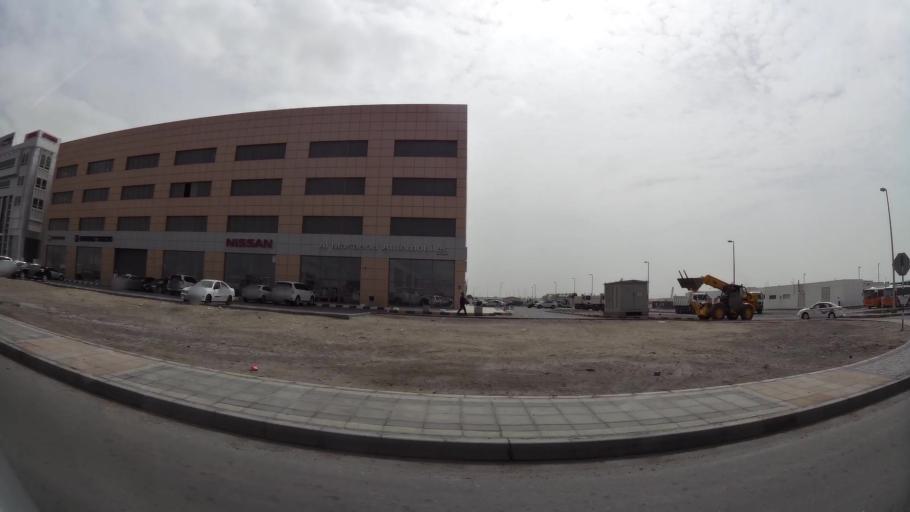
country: AE
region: Abu Dhabi
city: Abu Dhabi
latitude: 24.3579
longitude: 54.4753
